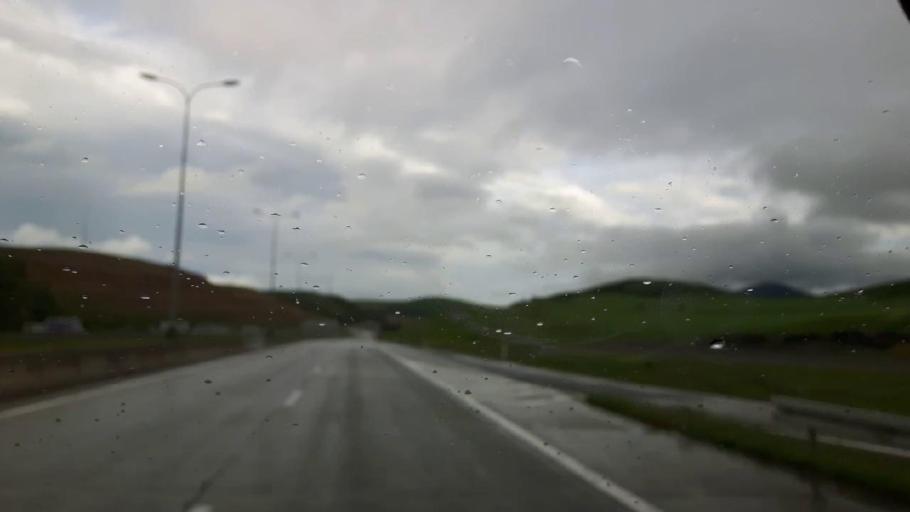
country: GE
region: Shida Kartli
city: Kaspi
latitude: 41.9990
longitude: 44.3933
